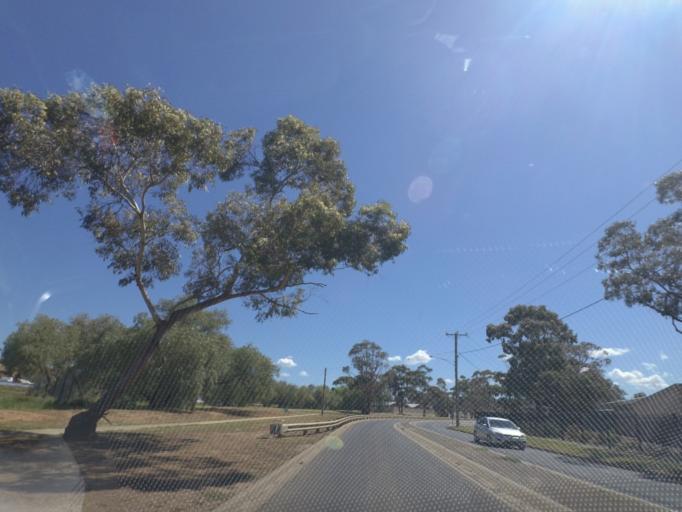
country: AU
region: Victoria
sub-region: Moorabool
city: Bacchus Marsh
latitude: -37.6865
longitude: 144.4325
